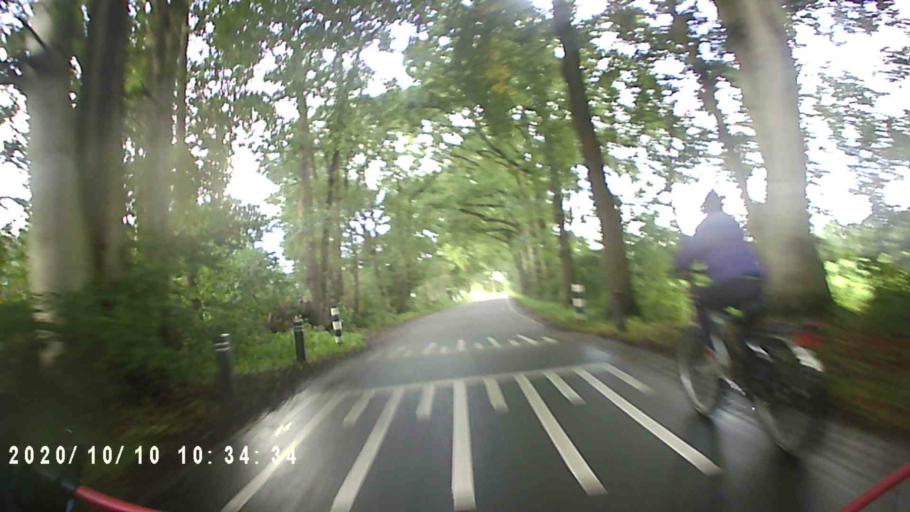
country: NL
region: Groningen
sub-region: Gemeente Grootegast
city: Grootegast
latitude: 53.1891
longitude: 6.3150
